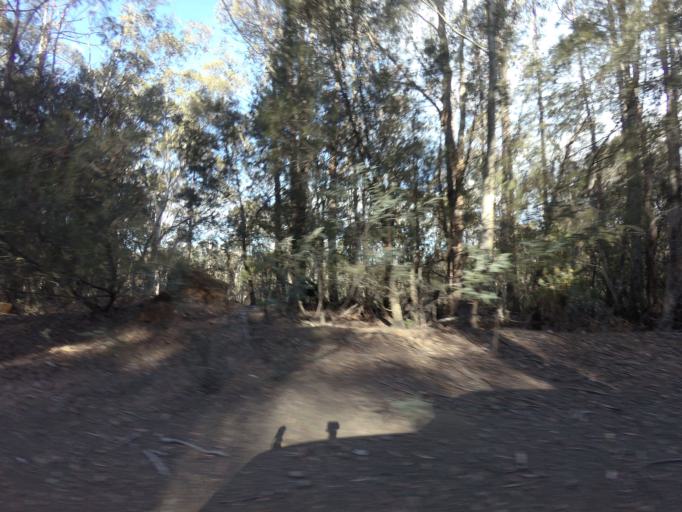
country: AU
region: Tasmania
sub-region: Break O'Day
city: St Helens
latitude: -41.8416
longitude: 148.0625
